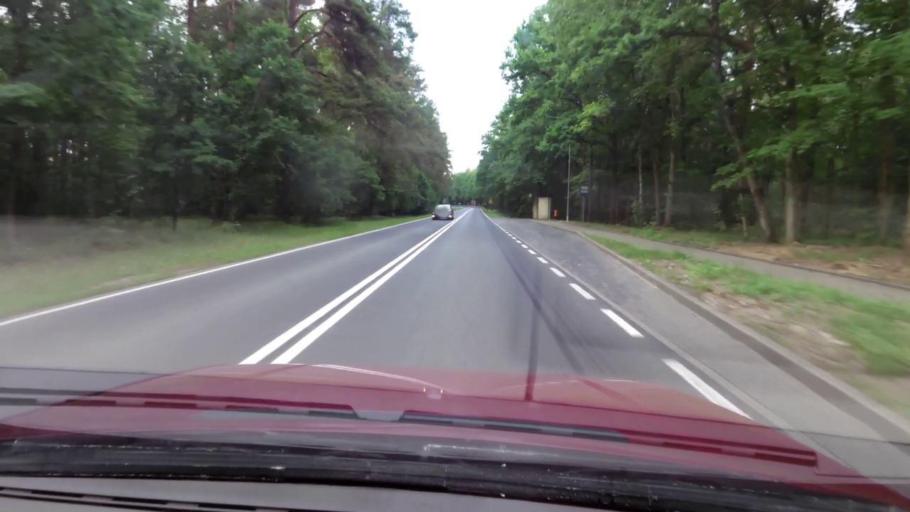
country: PL
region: Pomeranian Voivodeship
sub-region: Powiat bytowski
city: Trzebielino
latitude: 54.2522
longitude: 17.1031
